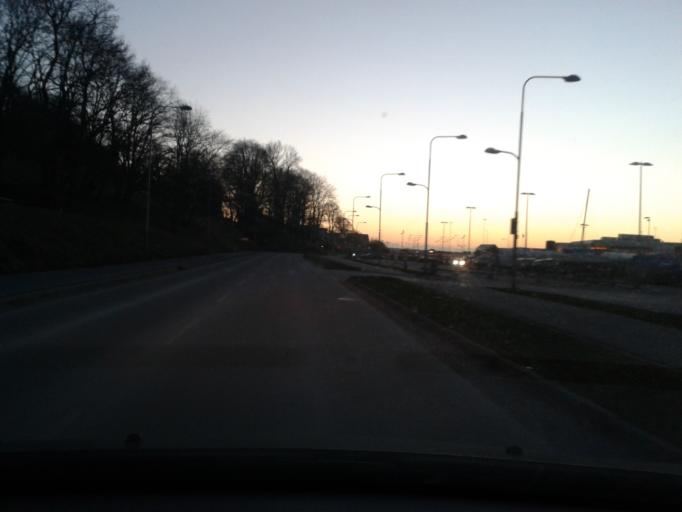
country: SE
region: Gotland
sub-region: Gotland
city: Visby
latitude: 57.6358
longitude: 18.2847
